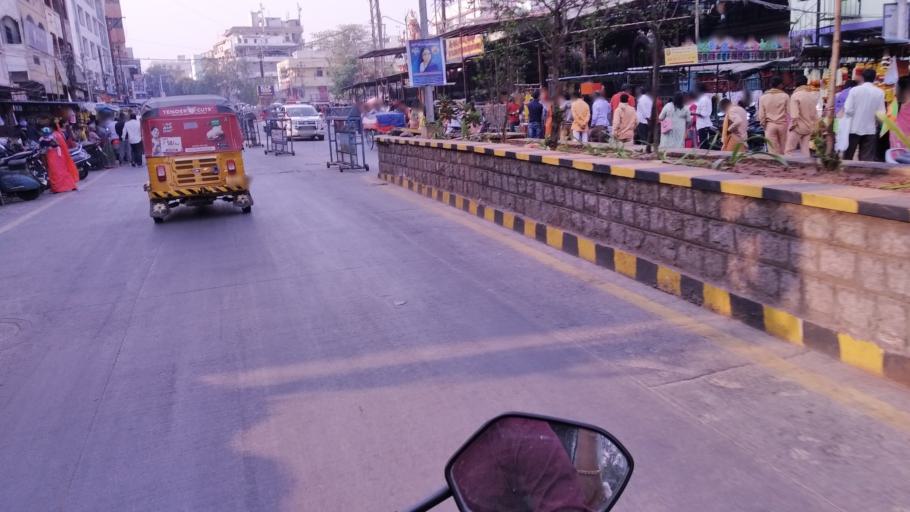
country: IN
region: Telangana
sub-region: Rangareddi
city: Kukatpalli
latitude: 17.4477
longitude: 78.4495
